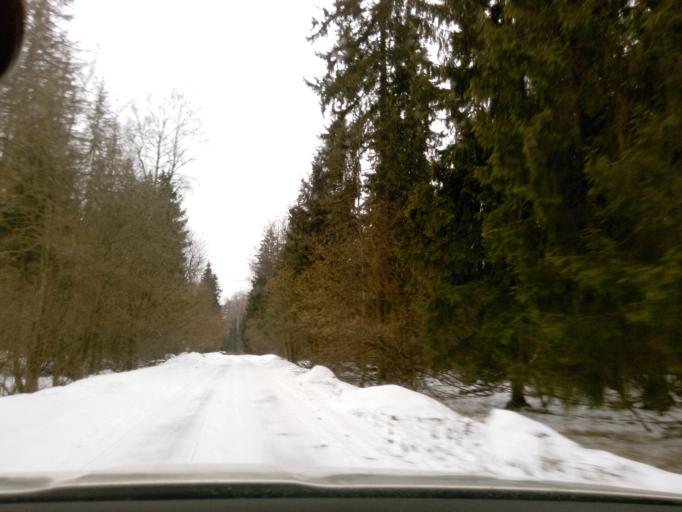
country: RU
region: Moskovskaya
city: Skhodnya
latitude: 55.9706
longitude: 37.2846
